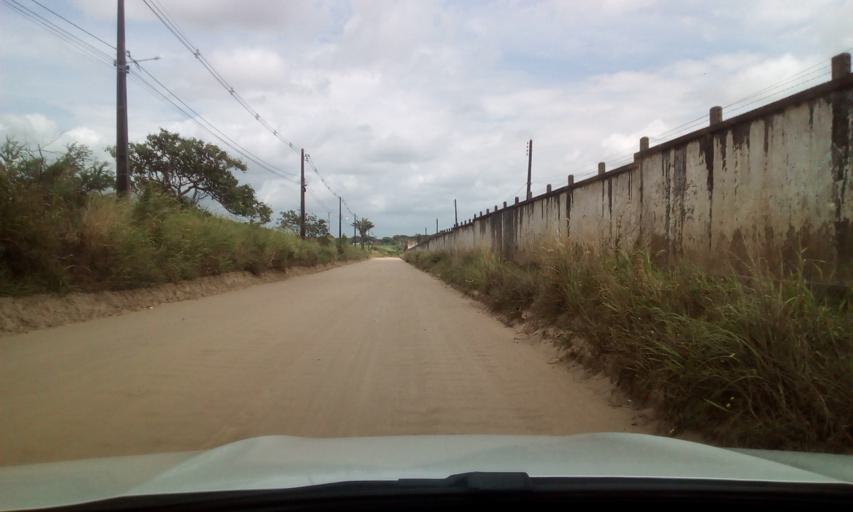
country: BR
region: Paraiba
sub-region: Bayeux
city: Bayeux
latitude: -7.1392
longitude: -34.9495
